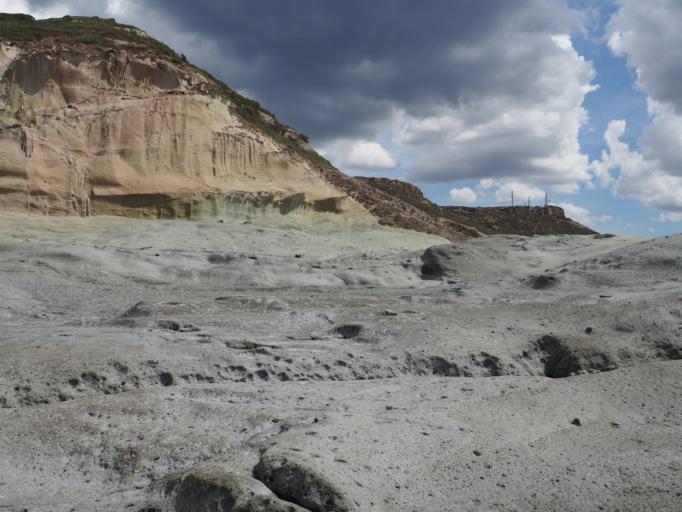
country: IT
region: Sardinia
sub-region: Provincia di Oristano
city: Bosa
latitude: 40.2948
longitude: 8.4688
